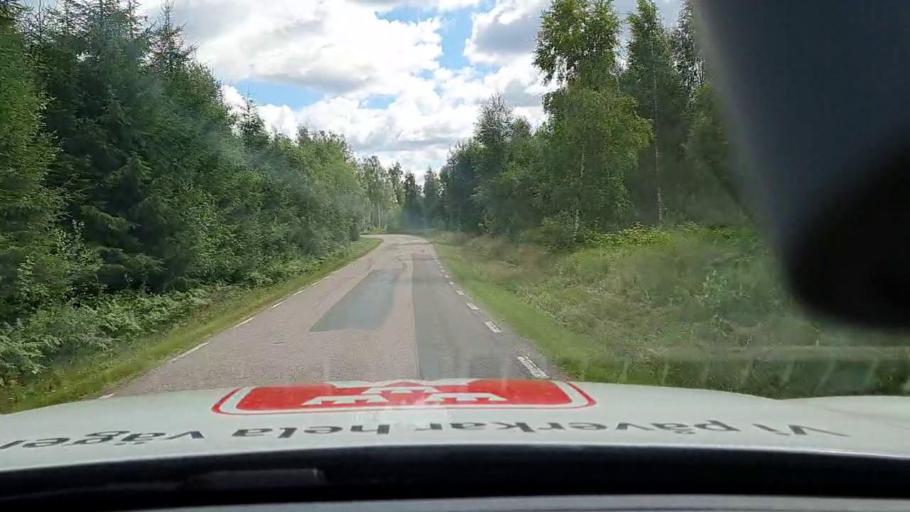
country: SE
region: Vaestra Goetaland
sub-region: Karlsborgs Kommun
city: Molltorp
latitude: 58.6055
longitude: 14.3022
